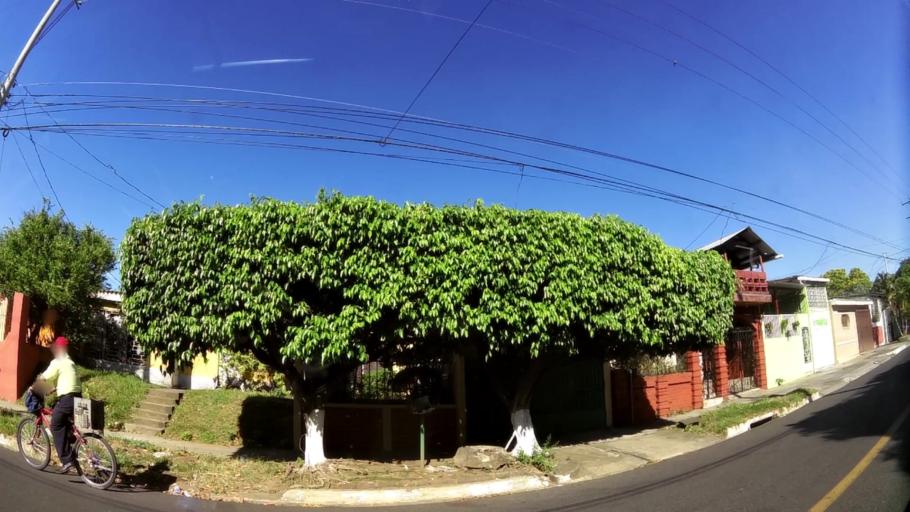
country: SV
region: Sonsonate
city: Sonzacate
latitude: 13.7294
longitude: -89.7172
